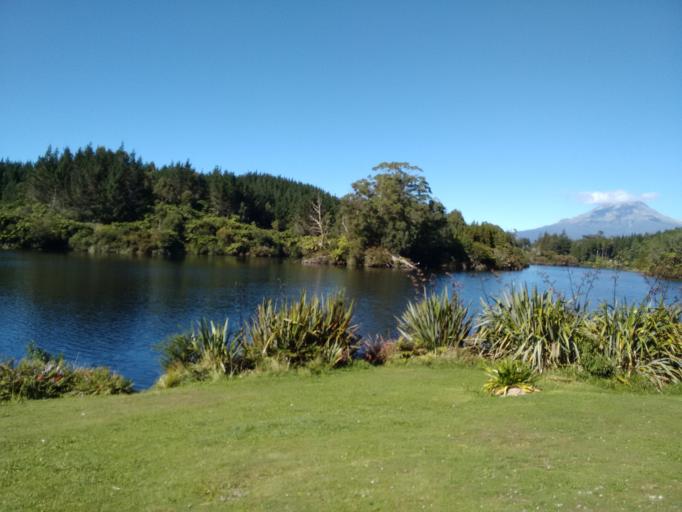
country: NZ
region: Taranaki
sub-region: New Plymouth District
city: New Plymouth
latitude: -39.1224
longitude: 174.1242
